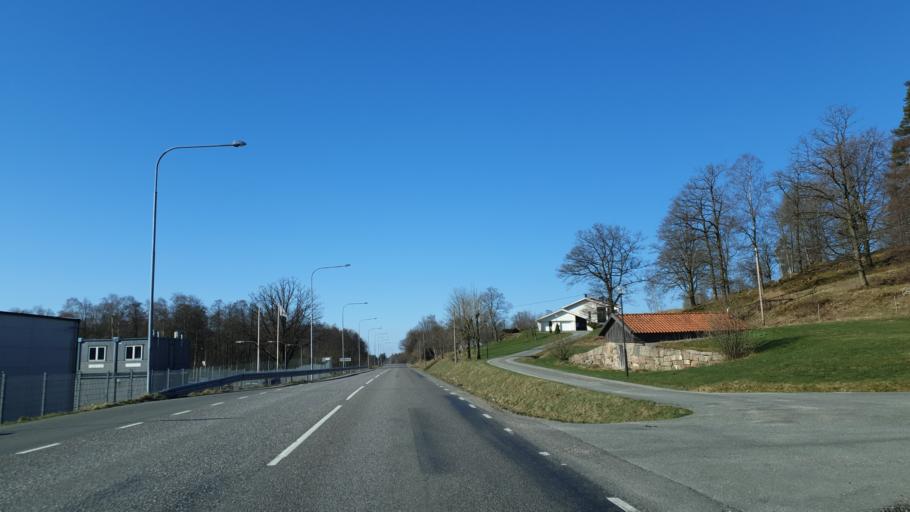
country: SE
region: Vaestra Goetaland
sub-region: Boras Kommun
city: Dalsjofors
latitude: 57.7041
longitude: 13.0673
